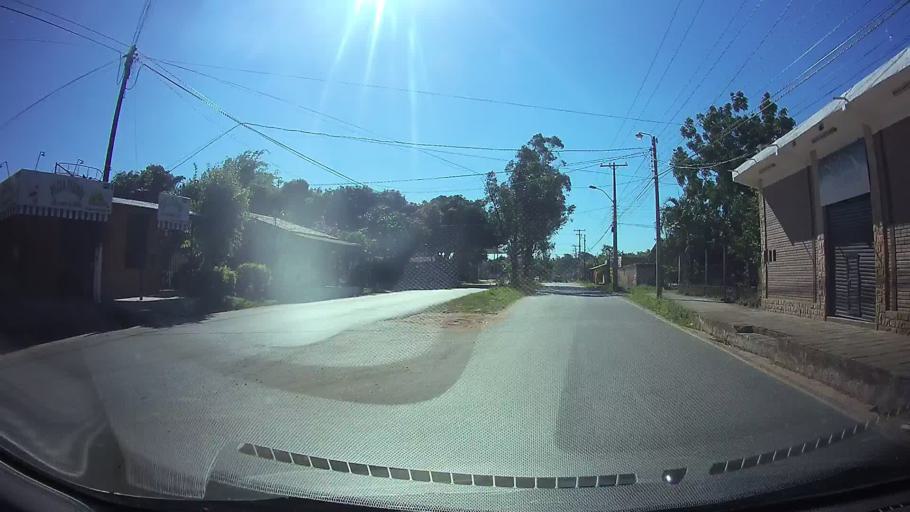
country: PY
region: Central
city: Fernando de la Mora
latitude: -25.2968
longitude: -57.5164
